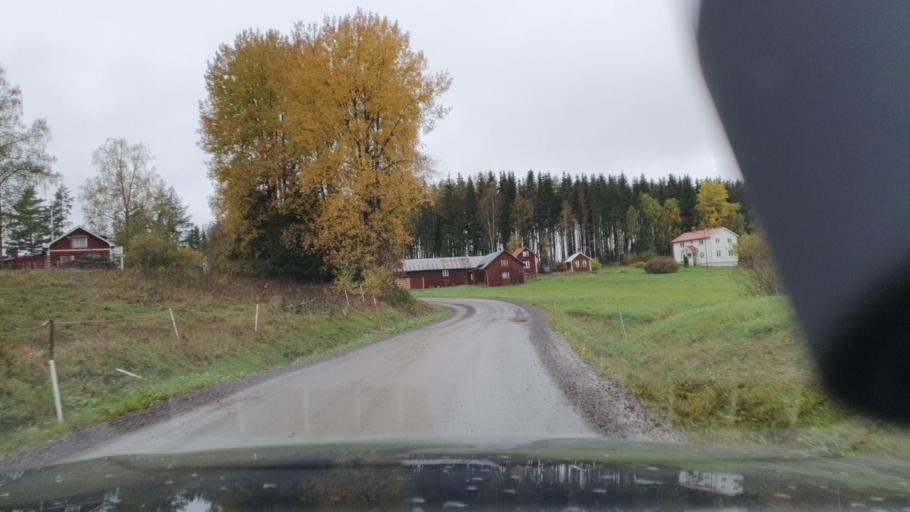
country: SE
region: Vaermland
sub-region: Eda Kommun
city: Amotfors
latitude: 59.7500
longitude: 12.4952
